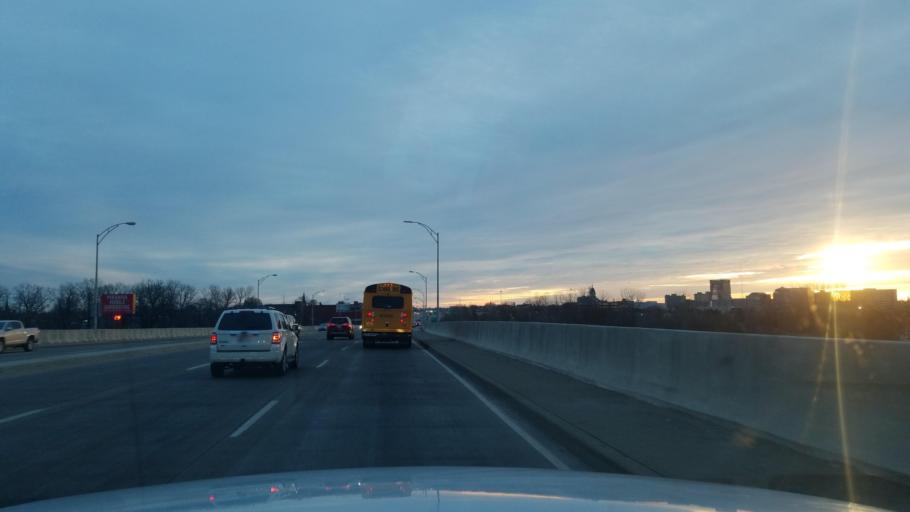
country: US
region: Indiana
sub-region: Vanderburgh County
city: Evansville
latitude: 37.9779
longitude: -87.5910
